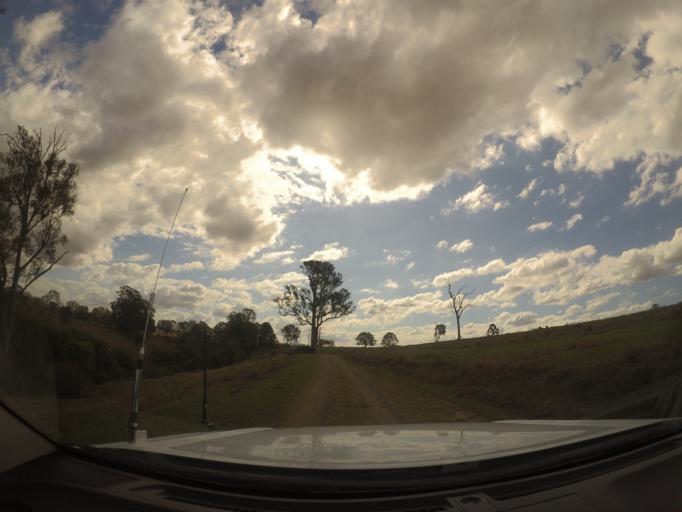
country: AU
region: Queensland
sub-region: Logan
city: North Maclean
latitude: -27.8091
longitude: 153.0094
